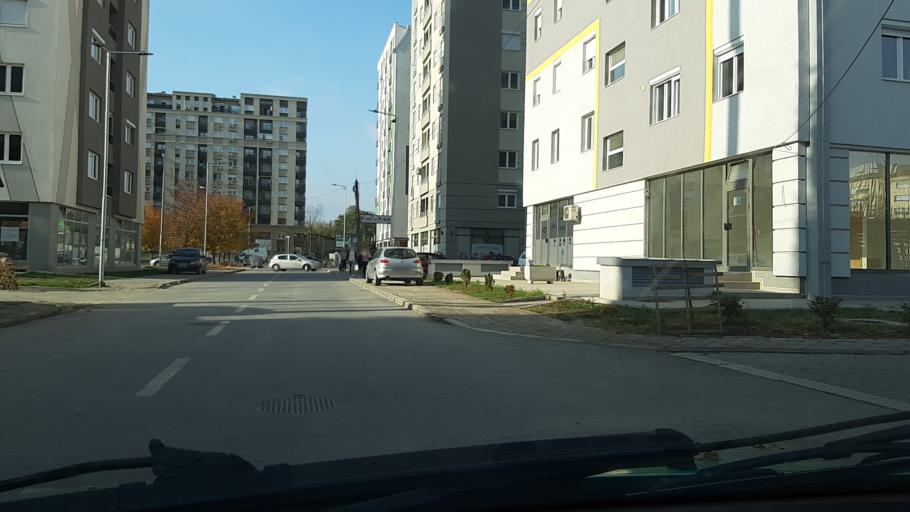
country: MK
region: Karpos
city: Skopje
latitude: 41.9849
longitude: 21.4527
